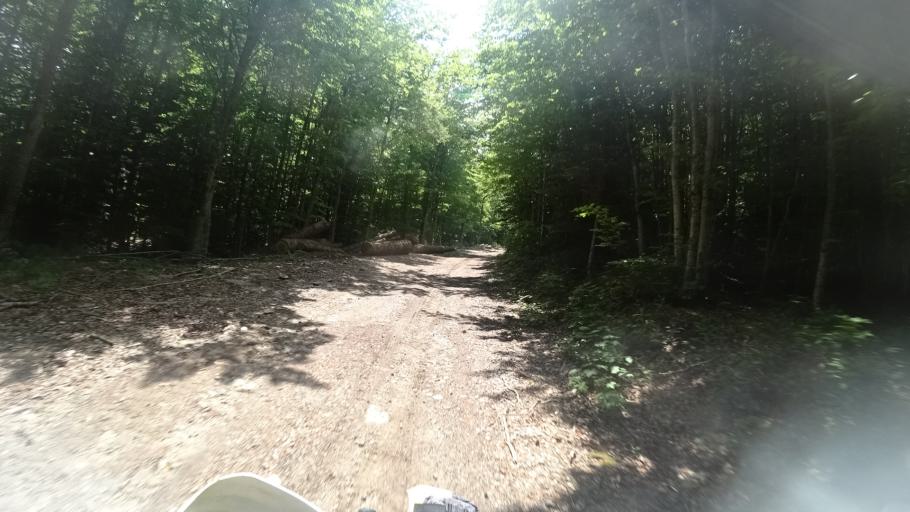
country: HR
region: Zadarska
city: Gracac
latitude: 44.4895
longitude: 15.8726
